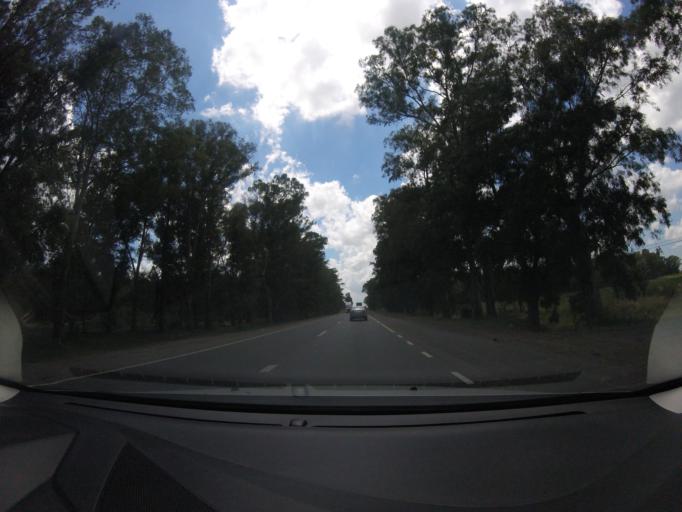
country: AR
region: Buenos Aires
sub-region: Partido de Las Flores
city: Las Flores
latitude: -36.0461
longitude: -59.0857
